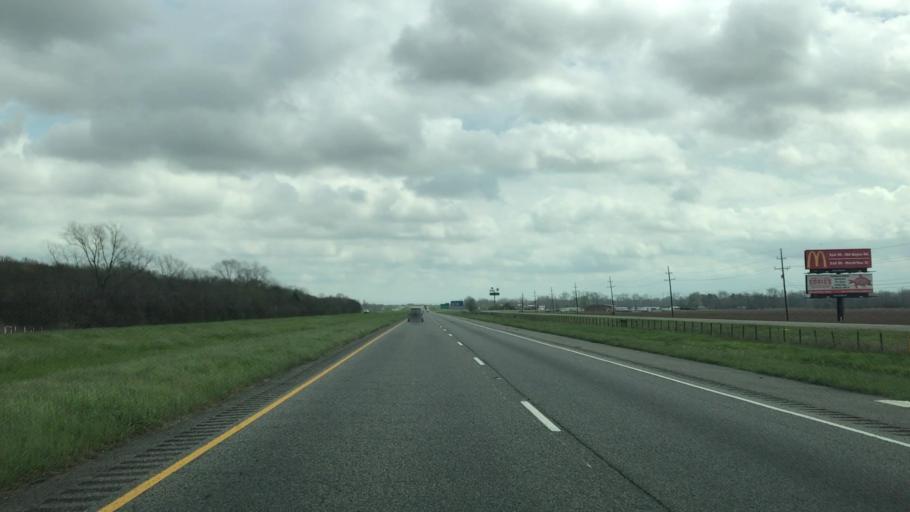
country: US
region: Louisiana
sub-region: Rapides Parish
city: Boyce
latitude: 31.3659
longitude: -92.6005
